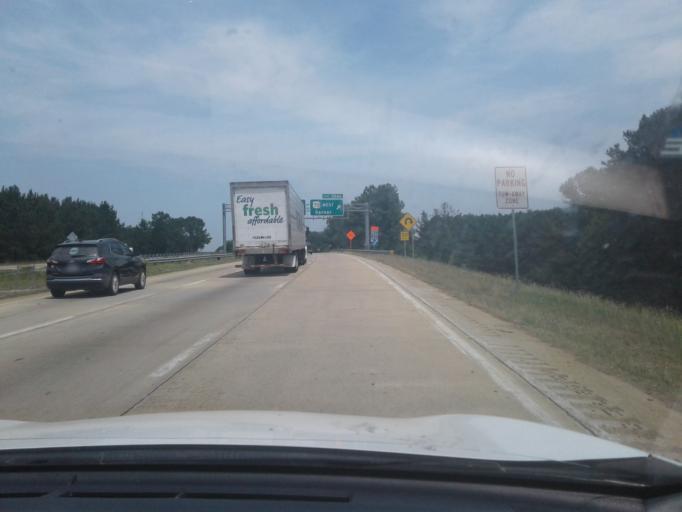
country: US
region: North Carolina
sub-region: Wake County
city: Garner
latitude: 35.6931
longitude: -78.5738
